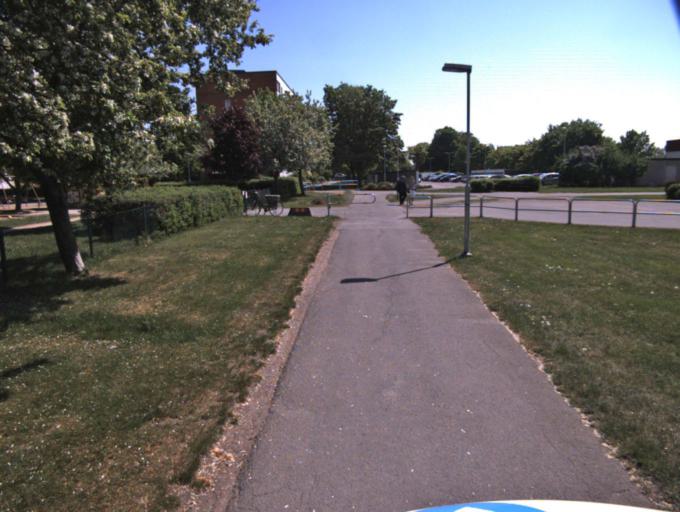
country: SE
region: Skane
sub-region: Kristianstads Kommun
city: Kristianstad
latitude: 56.0572
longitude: 14.1594
